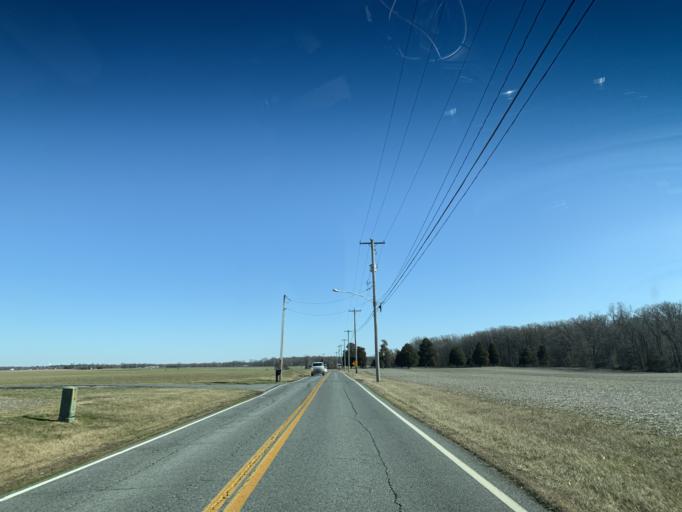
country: US
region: Maryland
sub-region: Cecil County
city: Elkton
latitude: 39.4914
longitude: -75.8783
